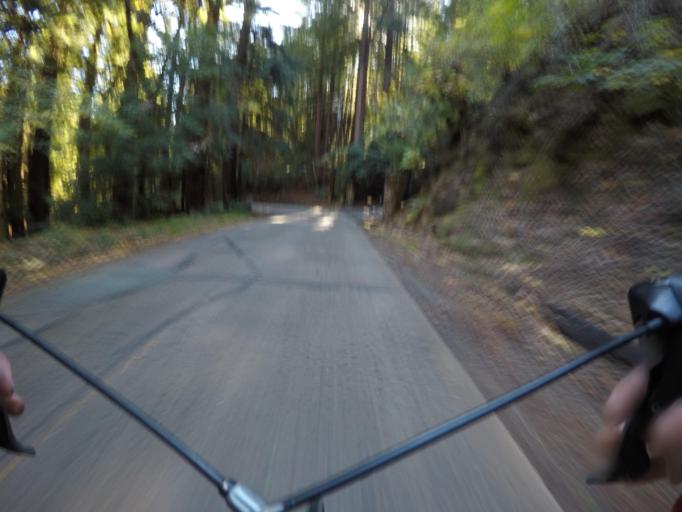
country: US
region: California
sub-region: Santa Clara County
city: Lexington Hills
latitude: 37.1151
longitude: -121.9873
